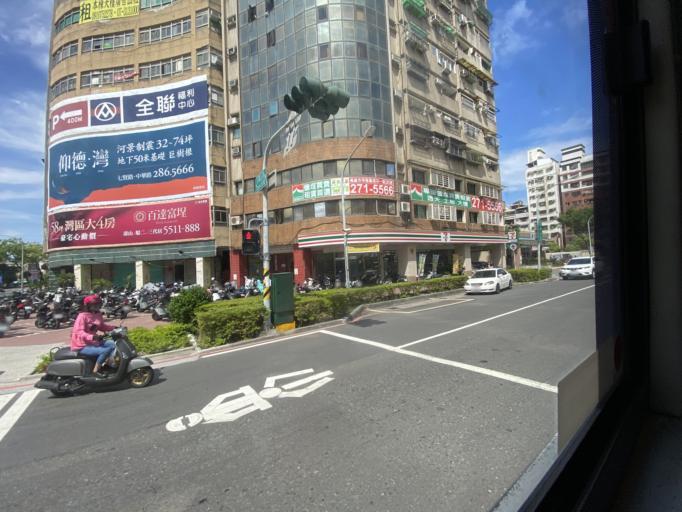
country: TW
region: Kaohsiung
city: Kaohsiung
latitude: 22.6247
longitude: 120.2813
